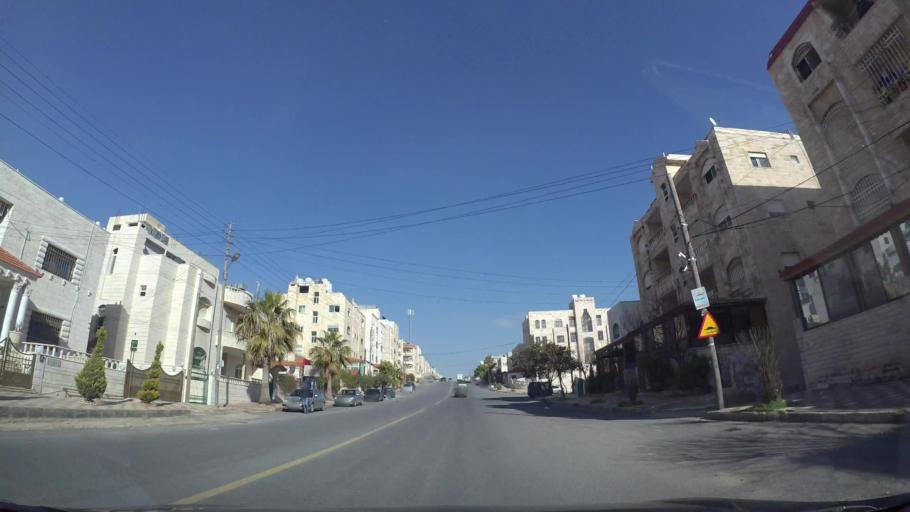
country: JO
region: Amman
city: Amman
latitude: 31.9870
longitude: 35.9339
